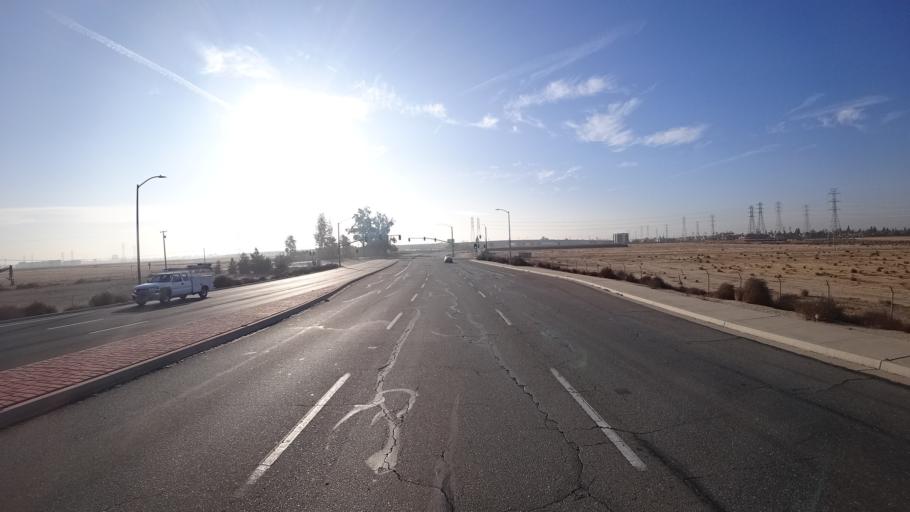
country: US
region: California
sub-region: Kern County
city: Greenacres
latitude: 35.3737
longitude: -119.0933
